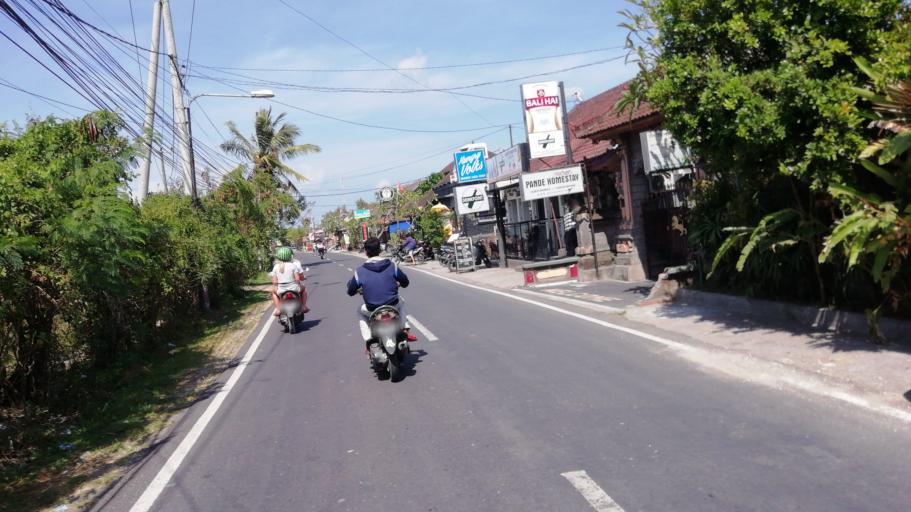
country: ID
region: Bali
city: Banjar Gunungpande
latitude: -8.6443
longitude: 115.1417
